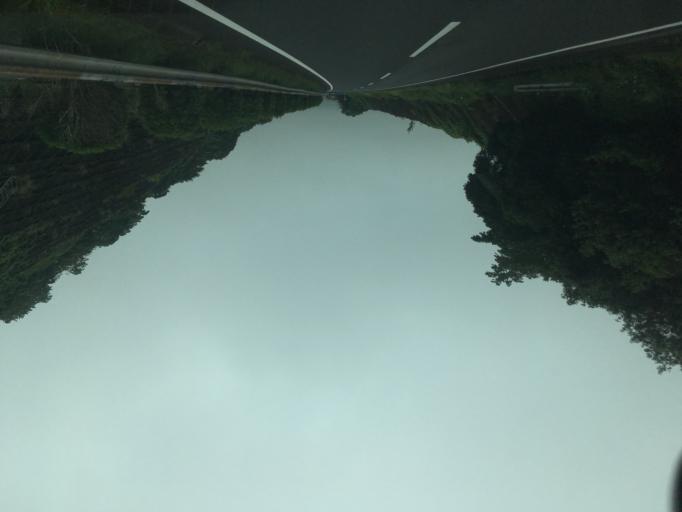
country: JP
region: Saga Prefecture
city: Saga-shi
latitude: 33.2864
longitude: 130.1547
